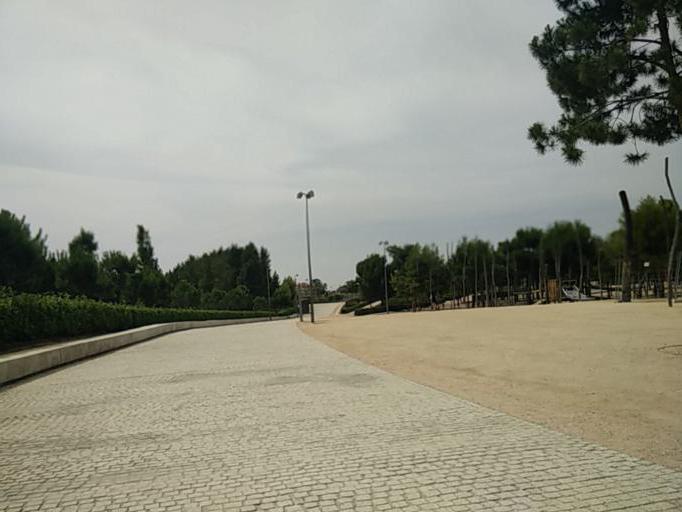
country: ES
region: Madrid
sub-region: Provincia de Madrid
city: Carabanchel
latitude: 40.3974
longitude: -3.7130
